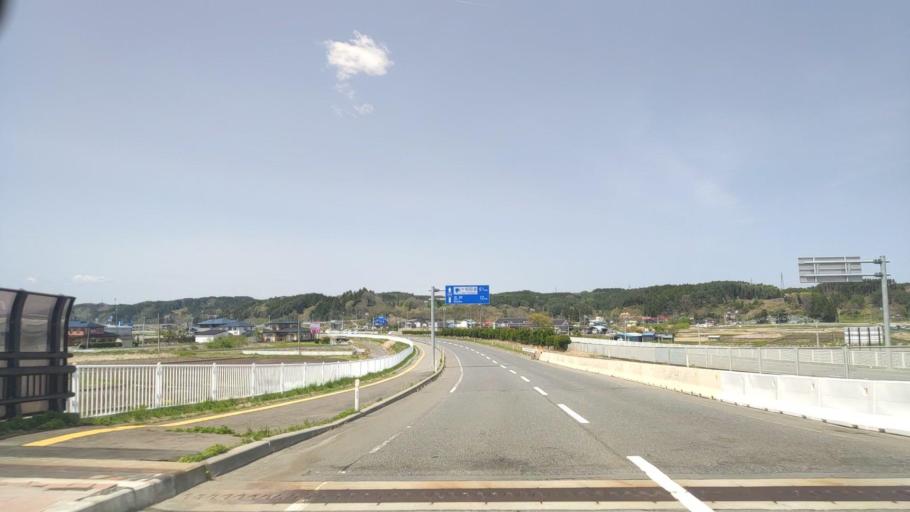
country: JP
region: Aomori
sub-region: Hachinohe Shi
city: Uchimaru
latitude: 40.5165
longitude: 141.4349
